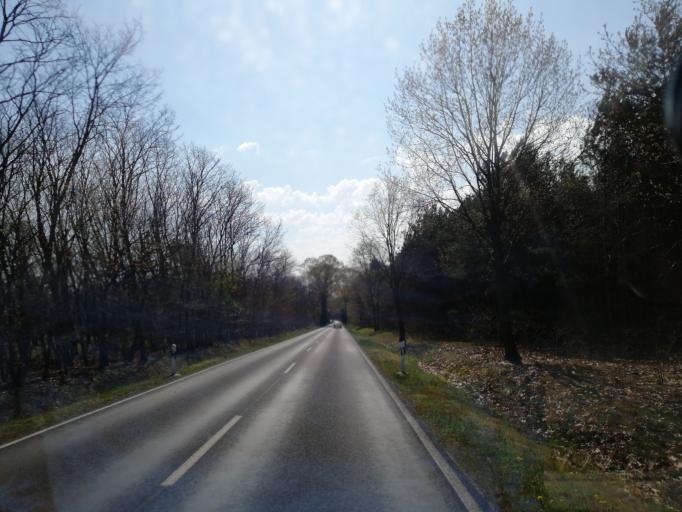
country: DE
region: Brandenburg
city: Calau
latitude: 51.7781
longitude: 13.8897
